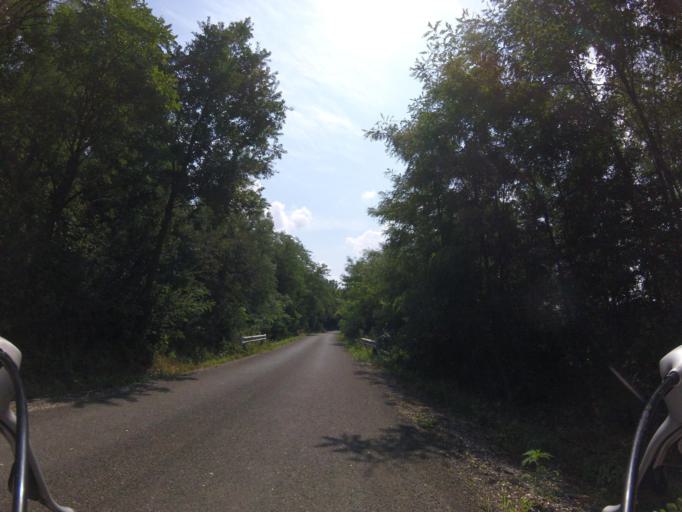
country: SK
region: Nitriansky
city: Sahy
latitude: 48.0172
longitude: 18.8228
